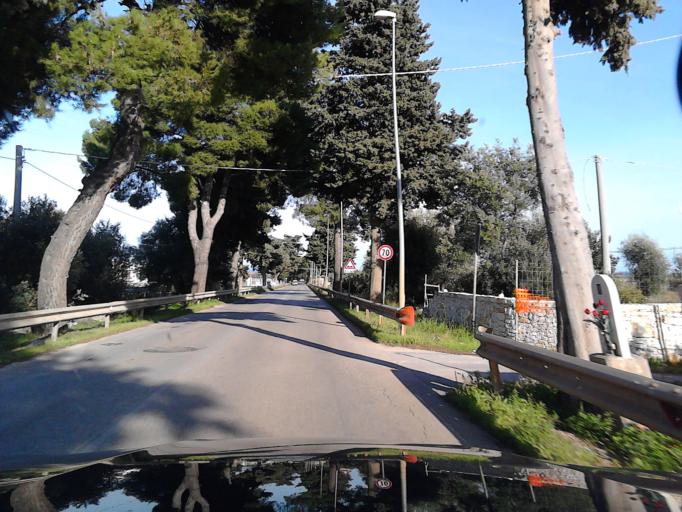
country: IT
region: Apulia
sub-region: Provincia di Bari
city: Mola di Bari
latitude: 41.0423
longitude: 17.0600
